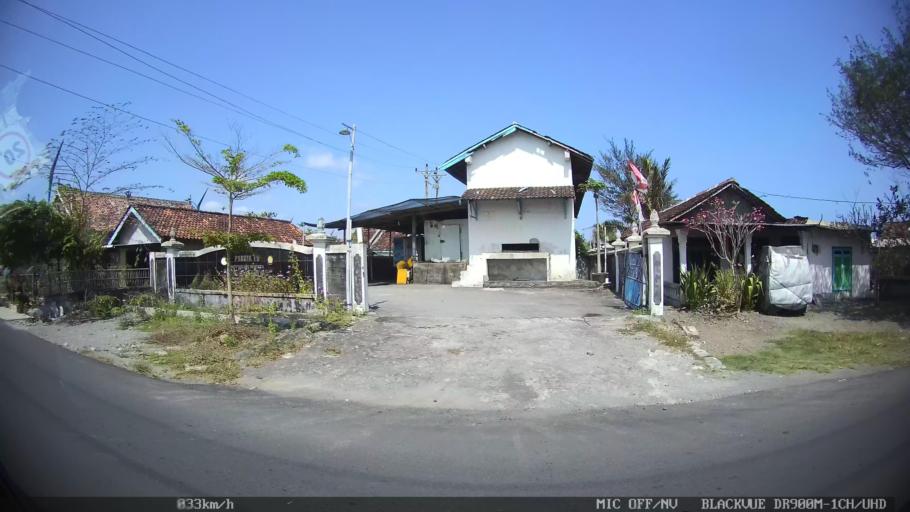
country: ID
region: Daerah Istimewa Yogyakarta
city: Bambanglipuro
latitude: -8.0117
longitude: 110.2942
